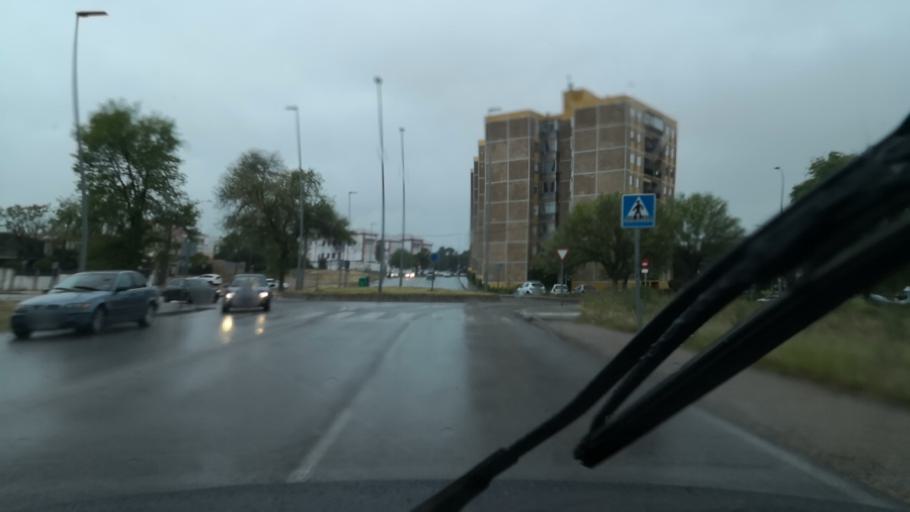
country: ES
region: Extremadura
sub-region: Provincia de Badajoz
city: Badajoz
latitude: 38.8861
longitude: -6.9895
